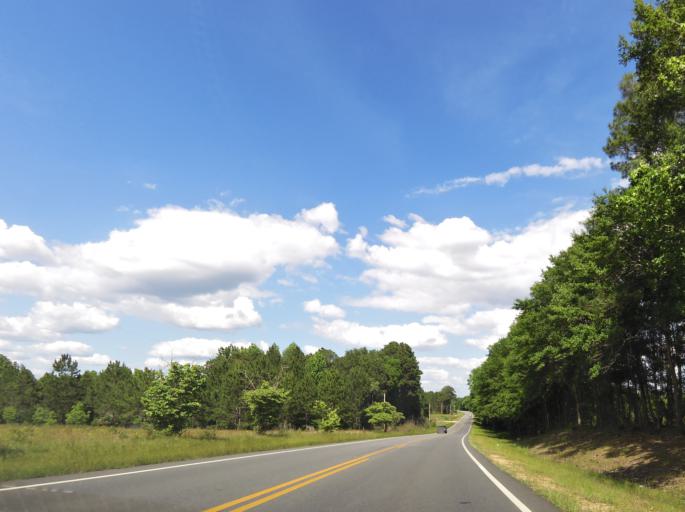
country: US
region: Georgia
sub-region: Treutlen County
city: Soperton
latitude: 32.3866
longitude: -82.5824
